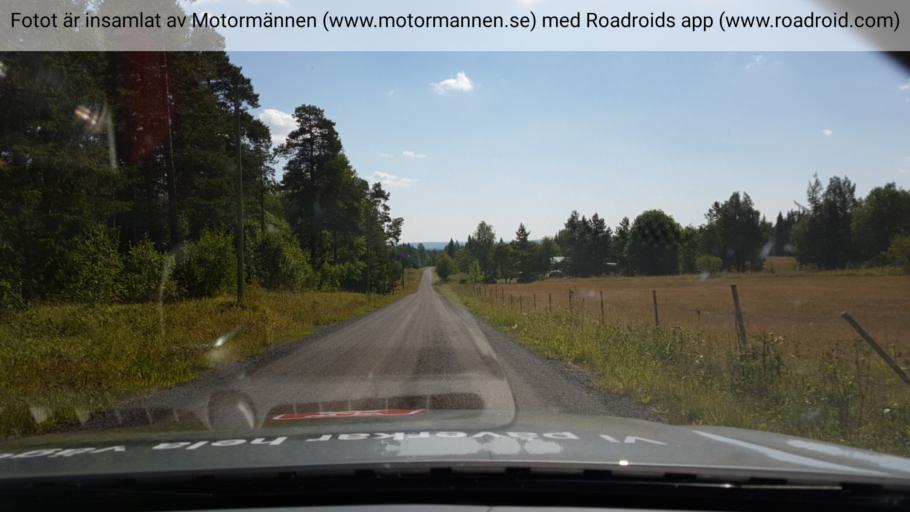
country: SE
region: Jaemtland
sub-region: OEstersunds Kommun
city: Lit
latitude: 63.3570
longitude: 15.2132
